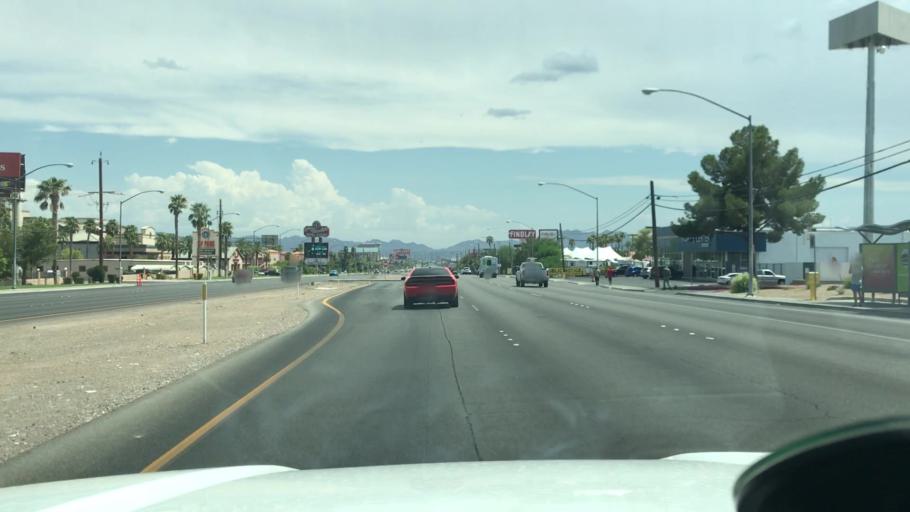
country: US
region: Nevada
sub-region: Clark County
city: Winchester
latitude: 36.1252
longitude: -115.0784
